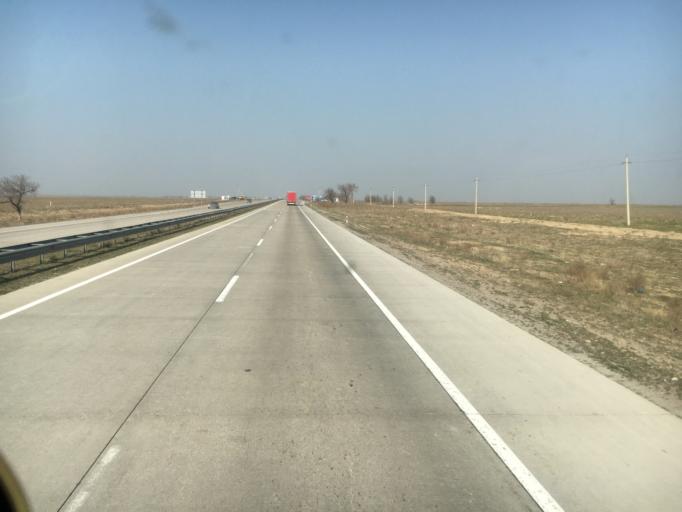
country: KZ
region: Ongtustik Qazaqstan
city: Temirlanovka
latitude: 42.8433
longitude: 69.1001
